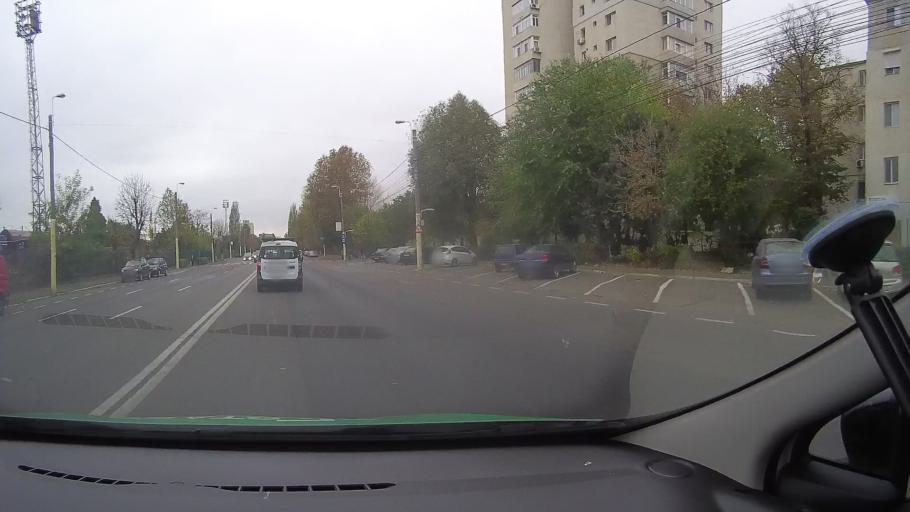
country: RO
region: Constanta
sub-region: Municipiul Constanta
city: Constanta
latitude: 44.1714
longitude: 28.6178
